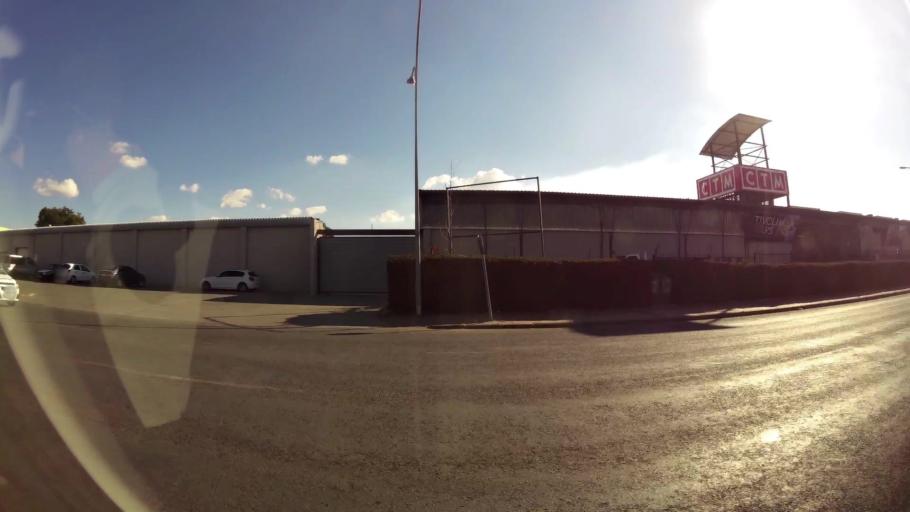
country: ZA
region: Northern Cape
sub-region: Frances Baard District Municipality
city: Kimberley
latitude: -28.7351
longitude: 24.7604
